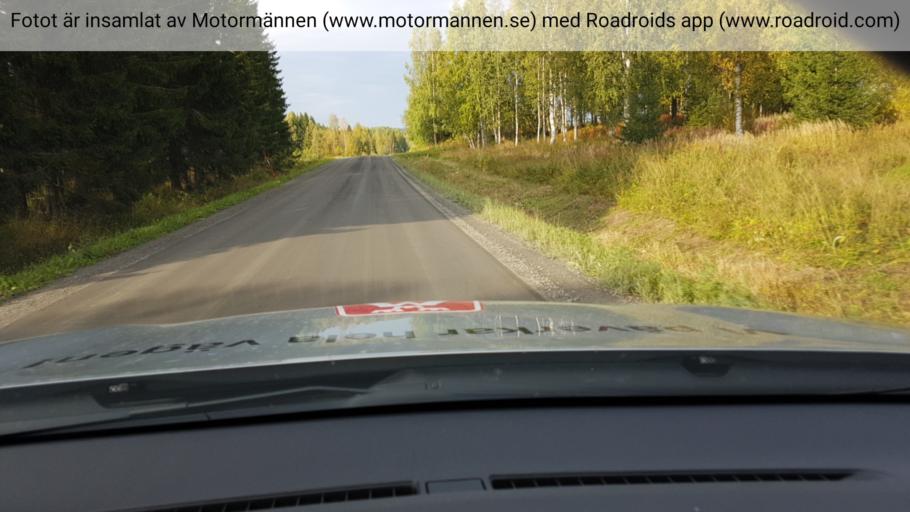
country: SE
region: Jaemtland
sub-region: Stroemsunds Kommun
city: Stroemsund
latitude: 64.0305
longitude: 15.8096
